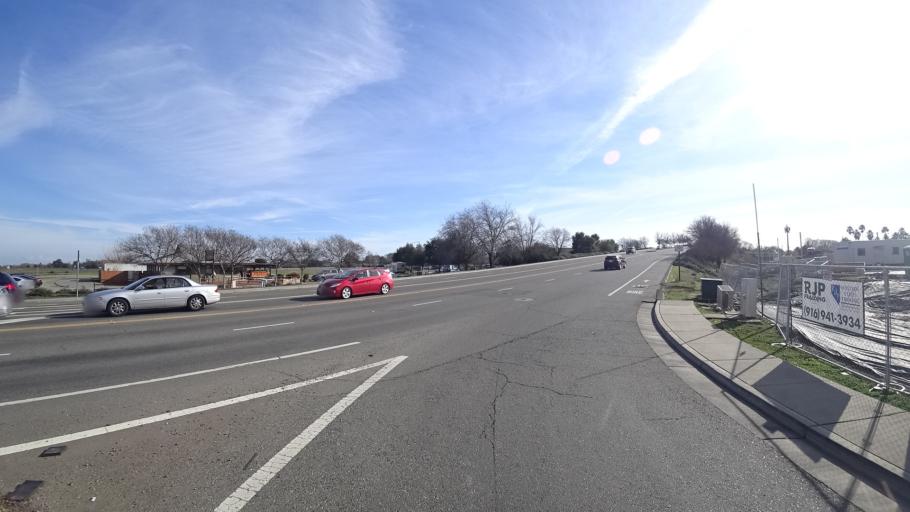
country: US
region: California
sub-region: Yolo County
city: Davis
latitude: 38.5563
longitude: -121.6943
